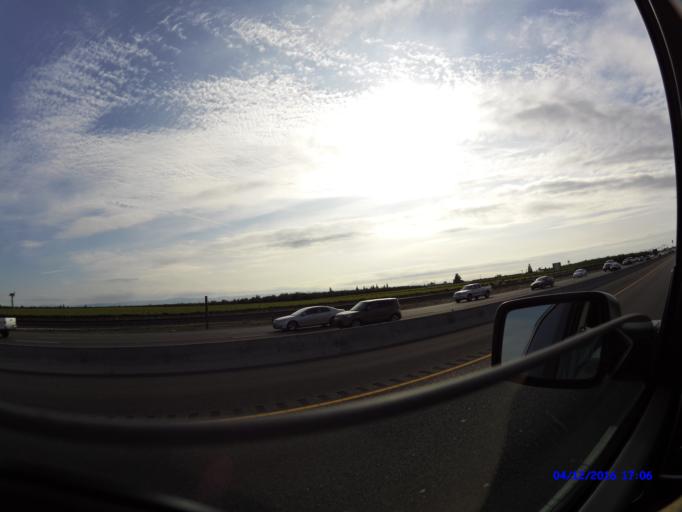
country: US
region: California
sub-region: San Joaquin County
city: Ripon
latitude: 37.7562
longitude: -121.1494
